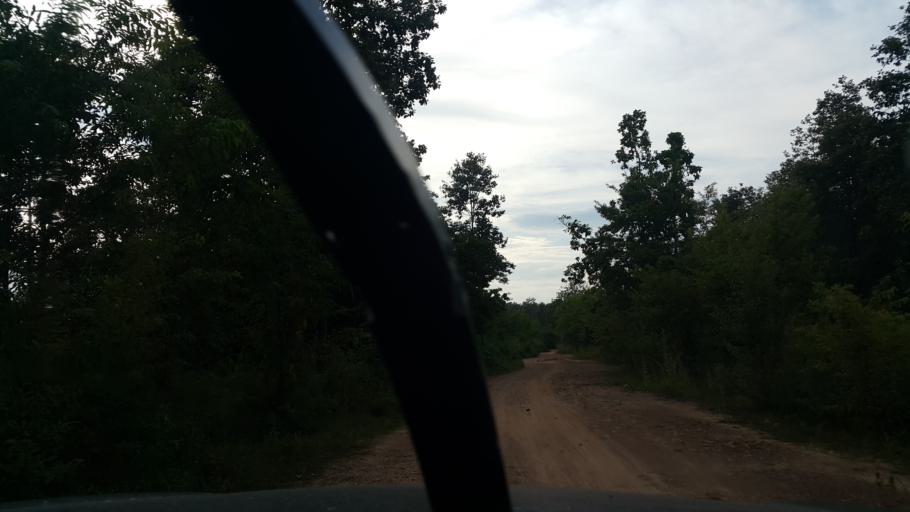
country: TH
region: Chiang Mai
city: San Sai
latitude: 18.9226
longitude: 99.0675
